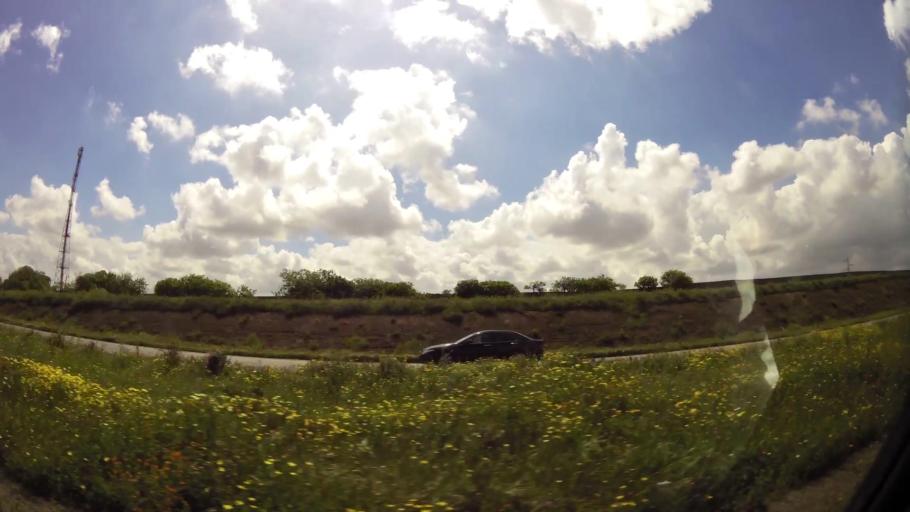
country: MA
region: Grand Casablanca
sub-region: Mediouna
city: Tit Mellil
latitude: 33.5512
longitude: -7.5188
